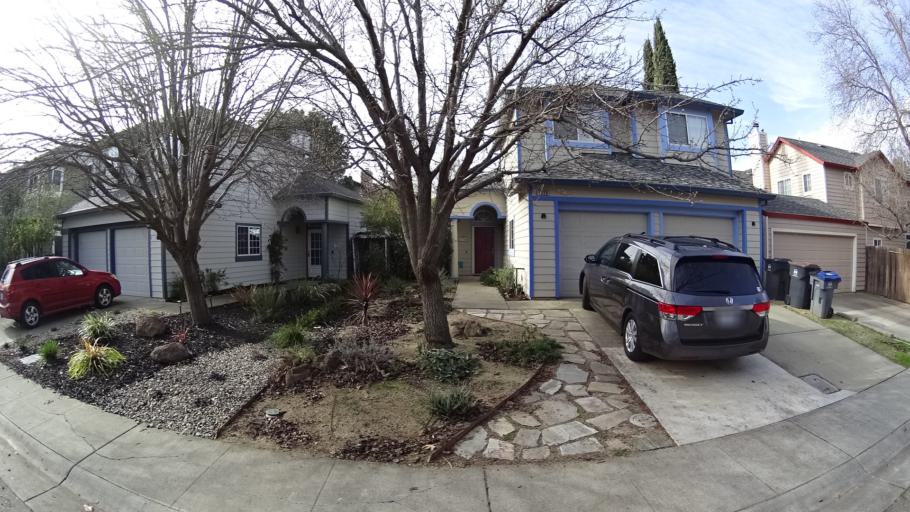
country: US
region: California
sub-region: Yolo County
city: Davis
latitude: 38.5426
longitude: -121.7213
